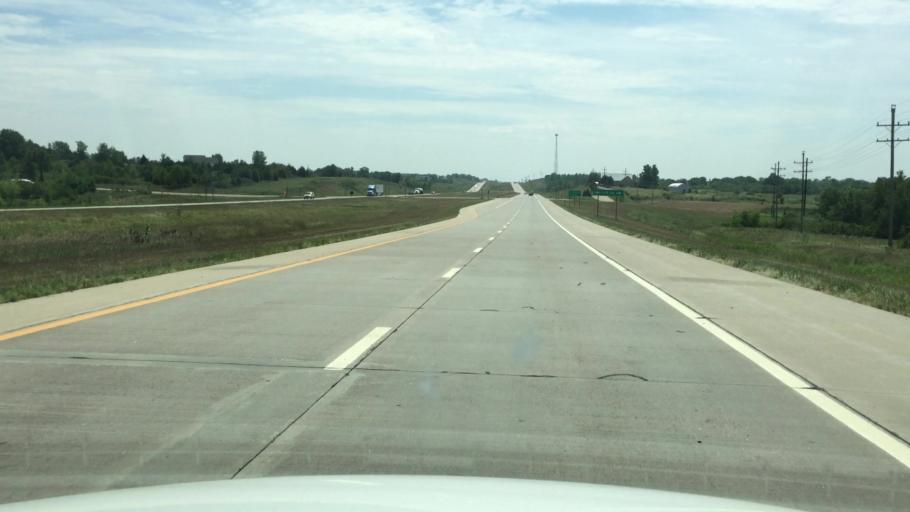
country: US
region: Kansas
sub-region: Jackson County
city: Holton
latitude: 39.2625
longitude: -95.7201
